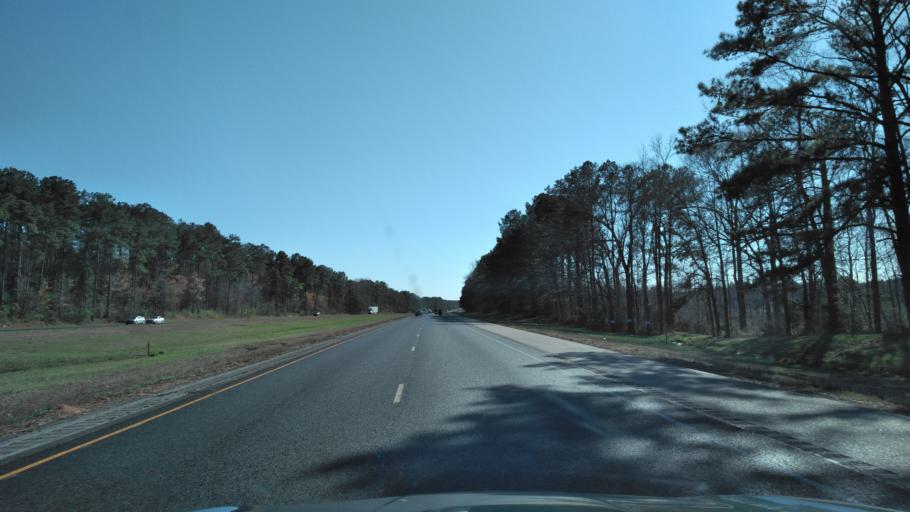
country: US
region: Alabama
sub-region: Butler County
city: Georgiana
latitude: 31.7461
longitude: -86.7108
